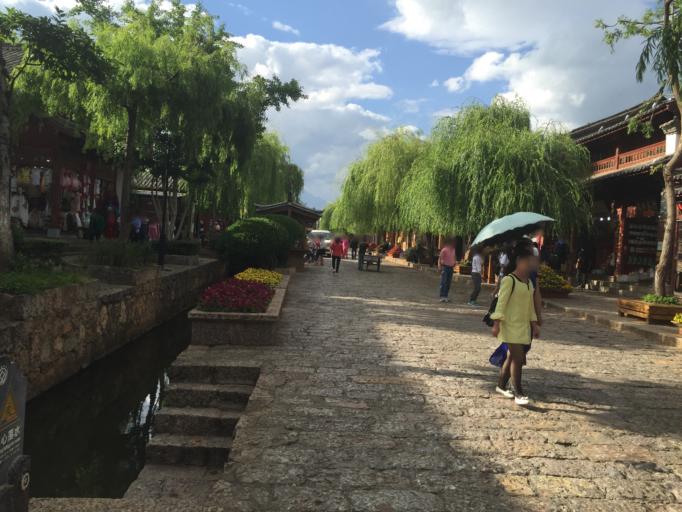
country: CN
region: Yunnan
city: Lijiang
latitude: 26.8781
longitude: 100.2326
